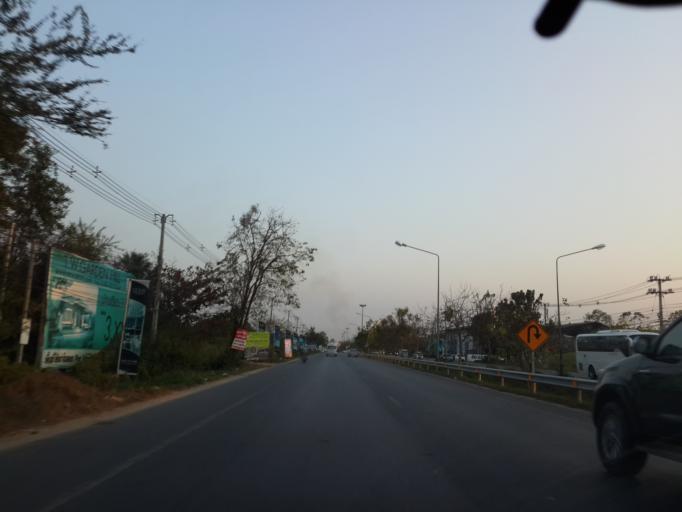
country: TH
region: Chon Buri
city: Phatthaya
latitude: 12.8312
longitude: 100.9141
